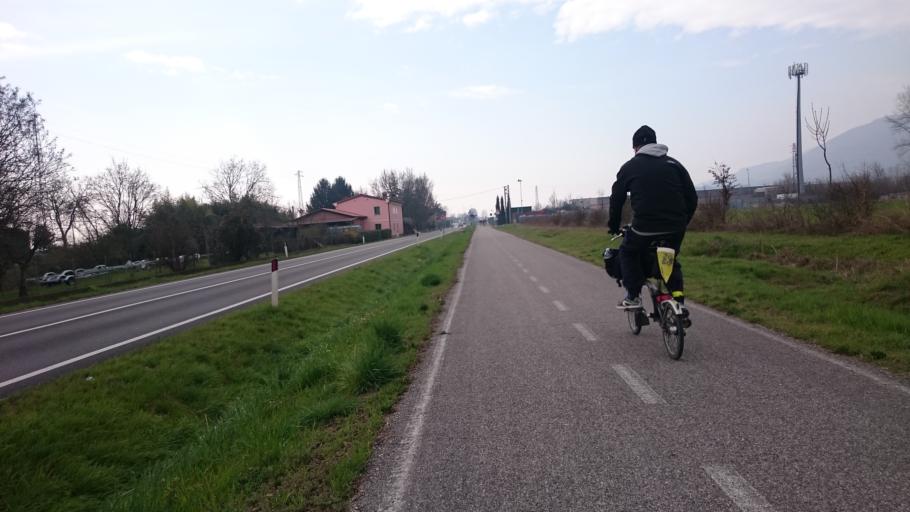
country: IT
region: Veneto
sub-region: Provincia di Vicenza
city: Longare
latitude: 45.4643
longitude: 11.6090
